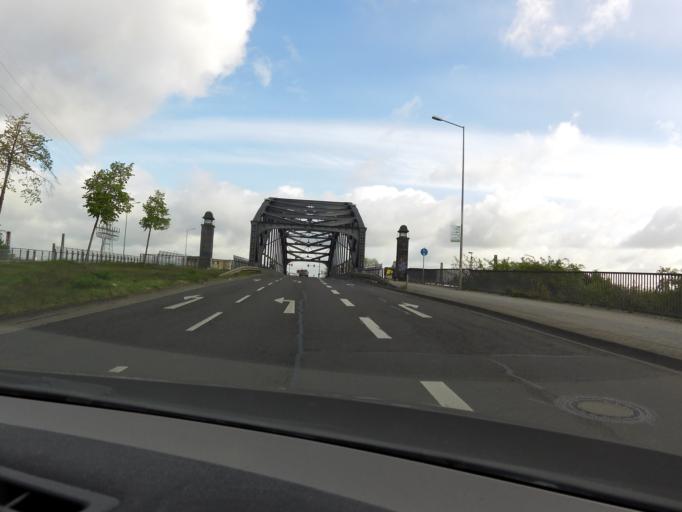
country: DE
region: Saxony
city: Leipzig
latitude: 51.3496
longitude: 12.3941
